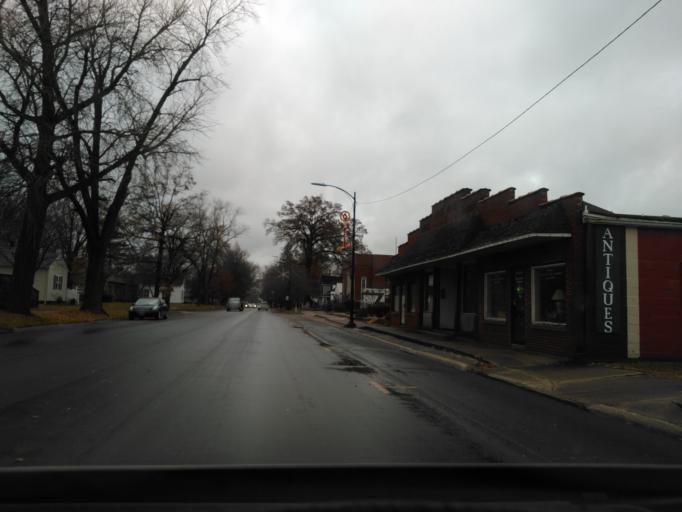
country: US
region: Illinois
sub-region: Effingham County
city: Altamont
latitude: 39.0593
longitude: -88.7480
